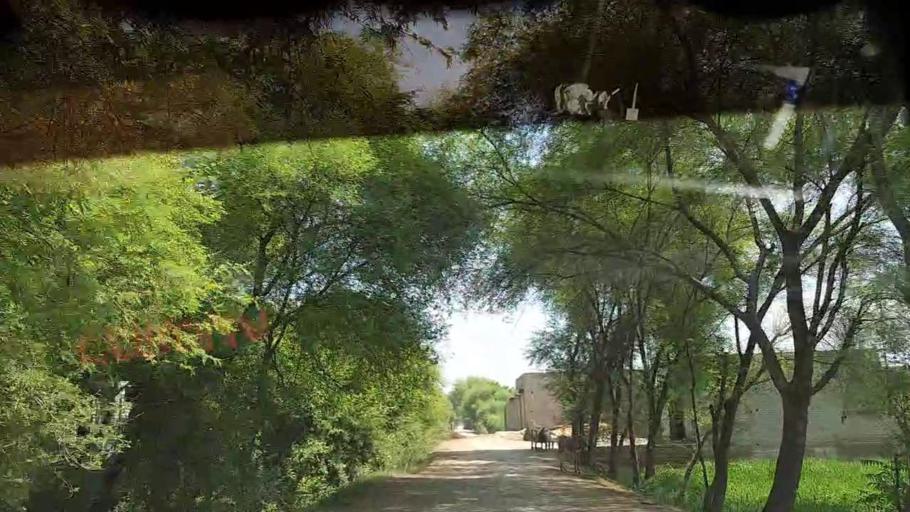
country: PK
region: Sindh
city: Ghauspur
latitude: 28.1719
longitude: 69.0599
